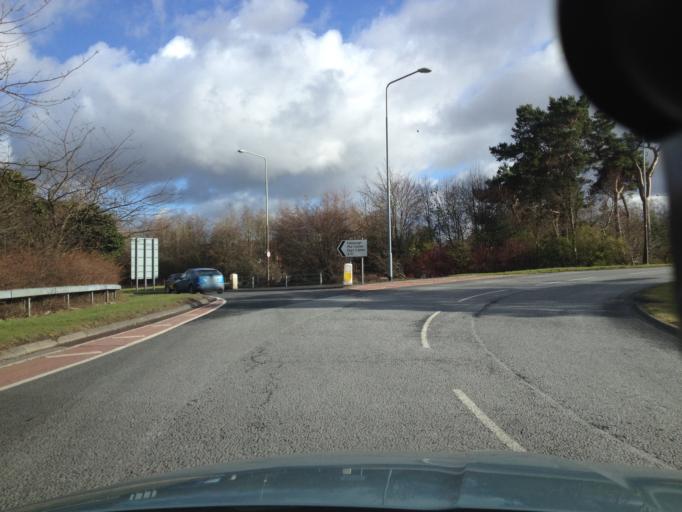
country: GB
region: Scotland
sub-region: West Lothian
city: Livingston
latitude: 55.8722
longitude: -3.5235
